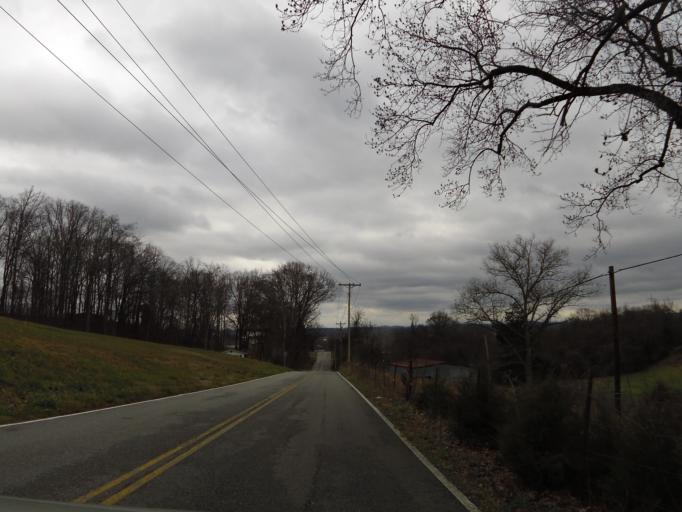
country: US
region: Tennessee
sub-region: Jefferson County
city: Jefferson City
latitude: 36.1895
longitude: -83.5045
